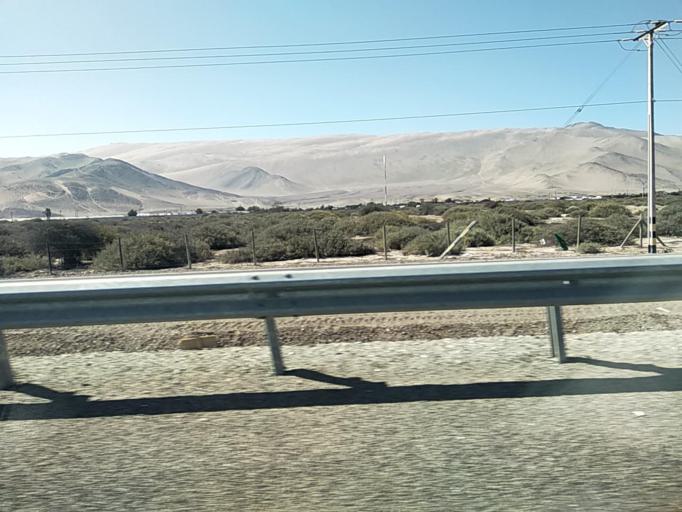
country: CL
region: Atacama
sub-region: Provincia de Copiapo
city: Copiapo
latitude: -27.2945
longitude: -70.4676
